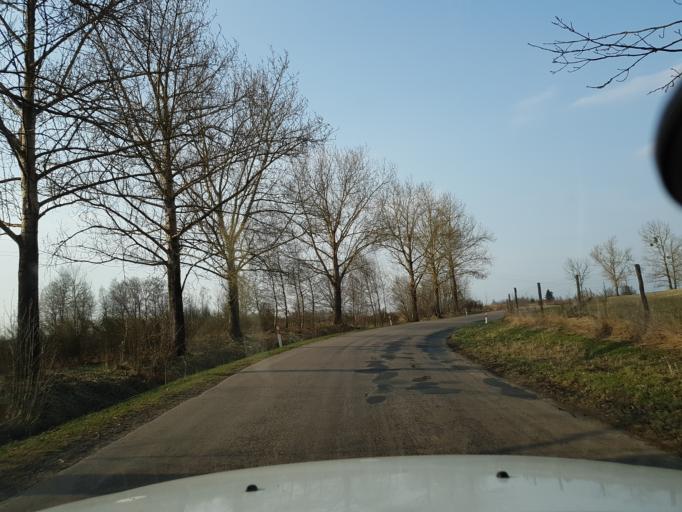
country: PL
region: West Pomeranian Voivodeship
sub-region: Powiat swidwinski
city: Polczyn-Zdroj
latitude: 53.7202
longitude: 16.0692
